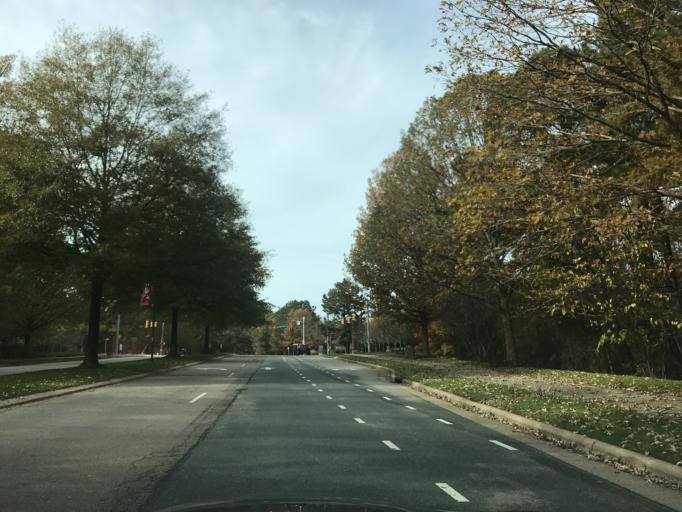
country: US
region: North Carolina
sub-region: Wake County
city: West Raleigh
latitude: 35.7749
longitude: -78.6797
